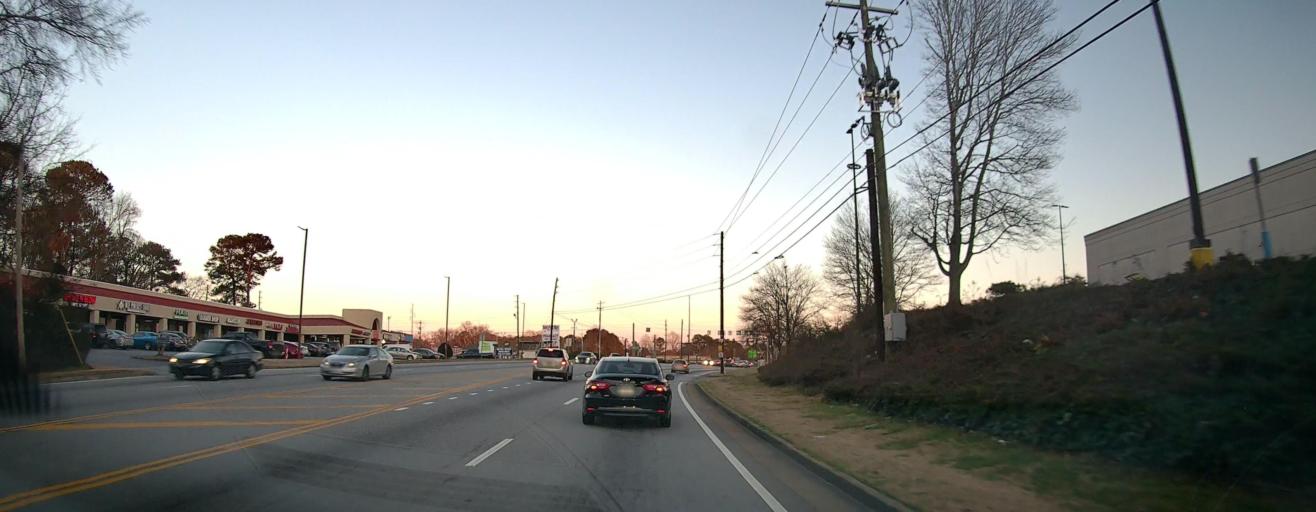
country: US
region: Georgia
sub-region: Clayton County
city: Riverdale
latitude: 33.5502
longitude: -84.4171
